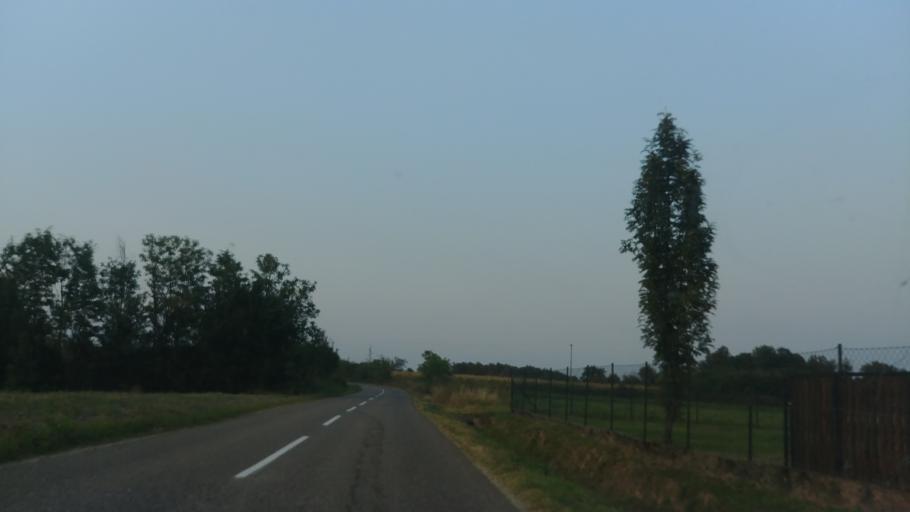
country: BA
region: Republika Srpska
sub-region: Opstina Ugljevik
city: Ugljevik
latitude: 44.7246
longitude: 18.9944
